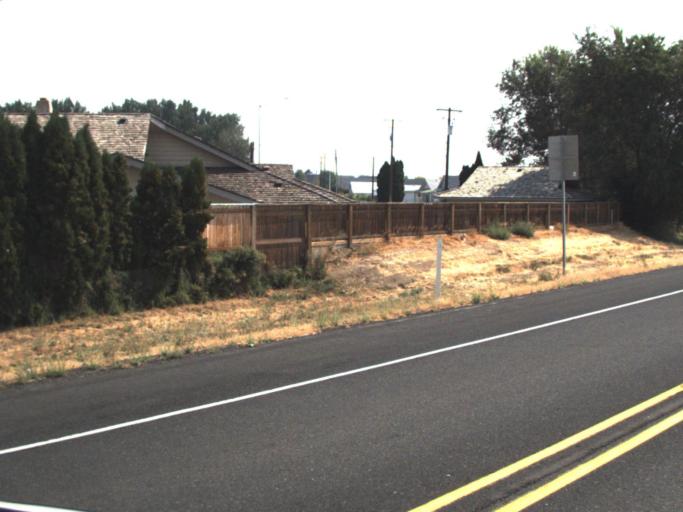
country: US
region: Washington
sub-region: Yakima County
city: Terrace Heights
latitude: 46.5514
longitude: -120.3890
